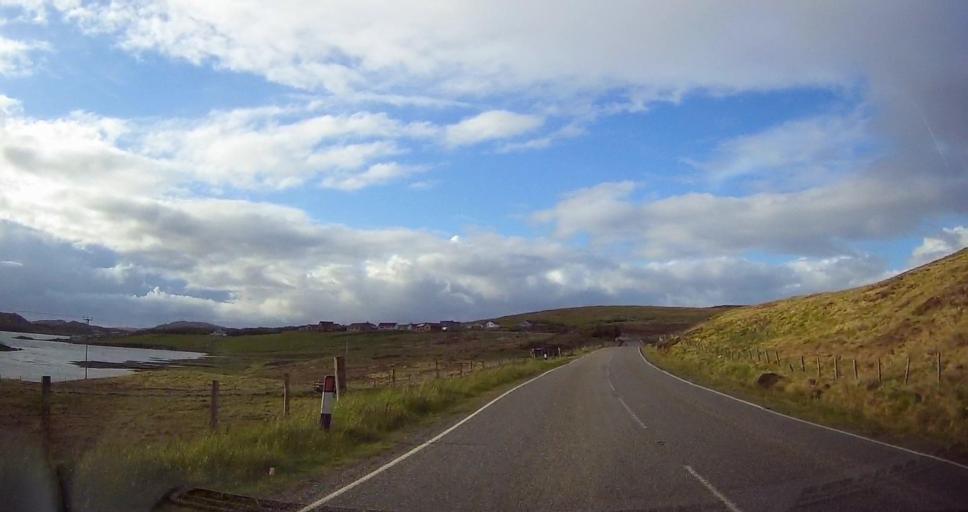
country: GB
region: Scotland
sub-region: Shetland Islands
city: Lerwick
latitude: 60.3818
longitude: -1.3430
